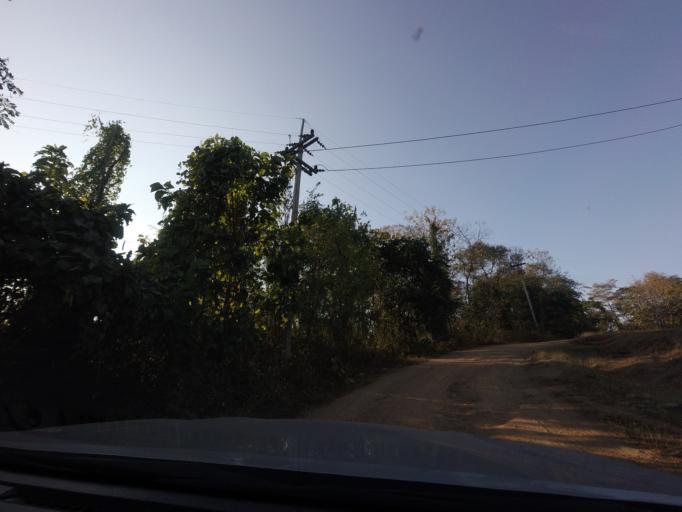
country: TH
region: Lampang
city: Mae Mo
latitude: 18.4127
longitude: 99.7453
